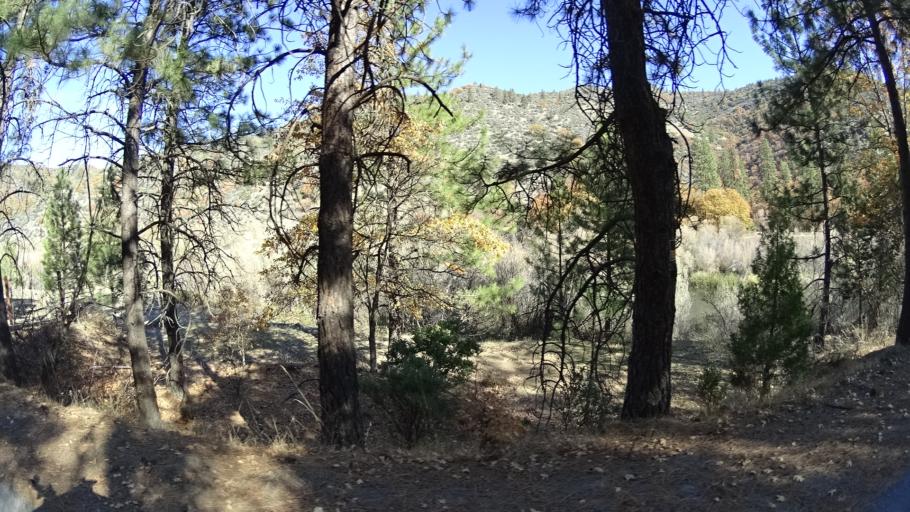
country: US
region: California
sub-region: Siskiyou County
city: Yreka
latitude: 41.8463
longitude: -122.6856
